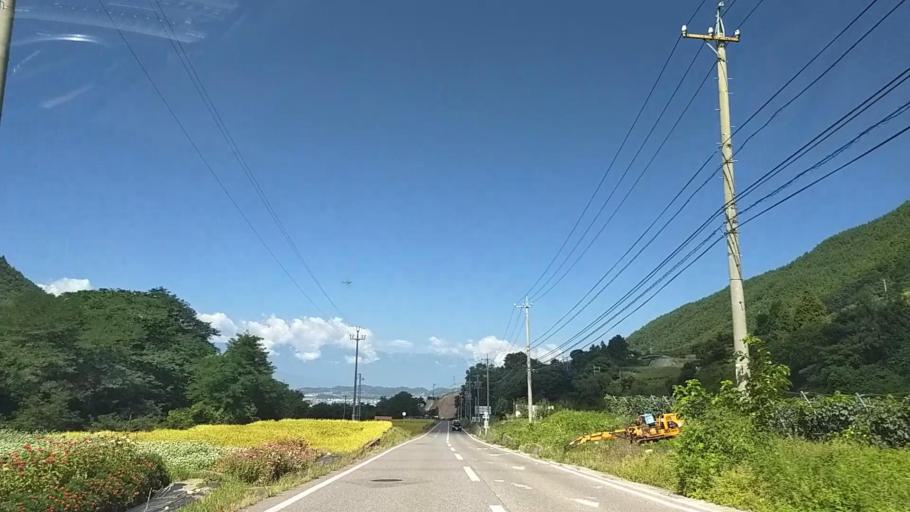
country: JP
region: Nagano
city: Matsumoto
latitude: 36.2237
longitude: 138.0353
